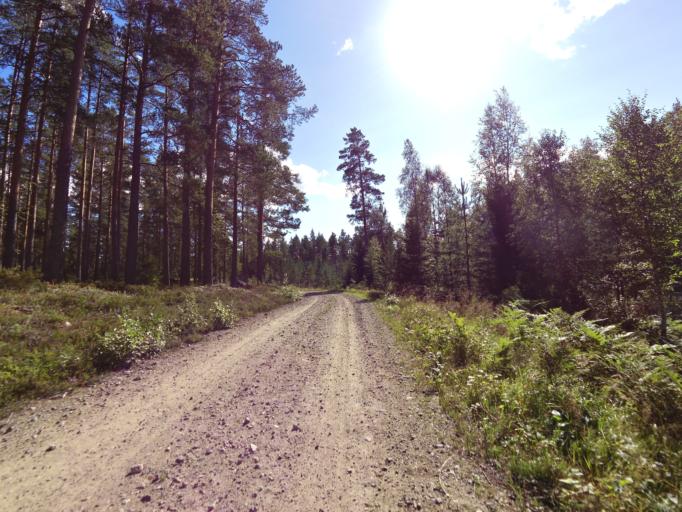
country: SE
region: Gaevleborg
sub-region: Ockelbo Kommun
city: Ockelbo
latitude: 60.8421
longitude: 16.7770
